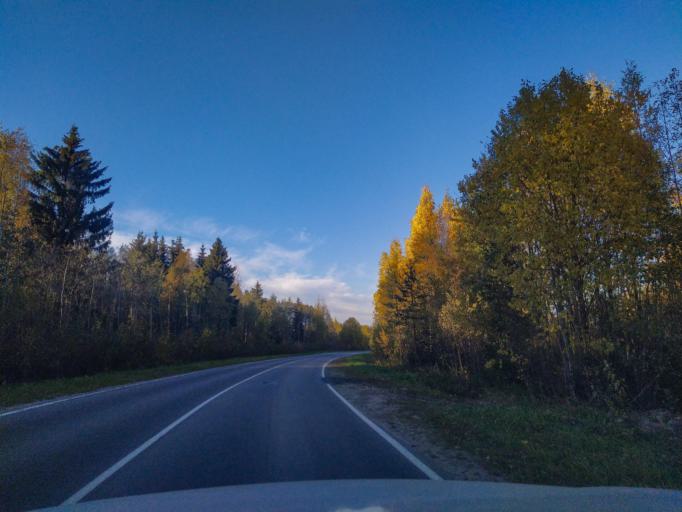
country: RU
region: Leningrad
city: Siverskiy
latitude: 59.3083
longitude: 30.0294
